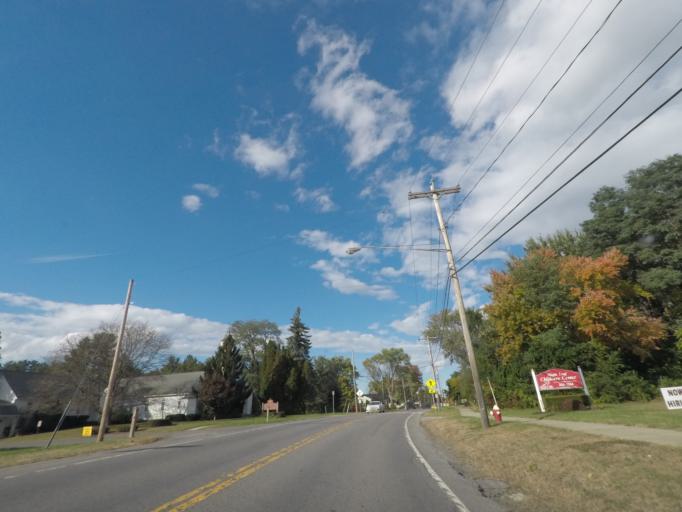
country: US
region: New York
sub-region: Schenectady County
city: Rotterdam
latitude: 42.7413
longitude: -73.9426
